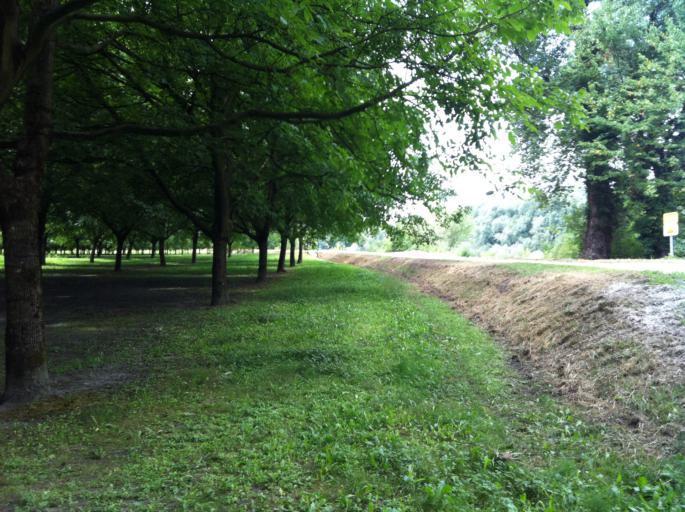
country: FR
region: Rhone-Alpes
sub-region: Departement de l'Isere
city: Autrans
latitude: 45.2203
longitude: 5.4858
